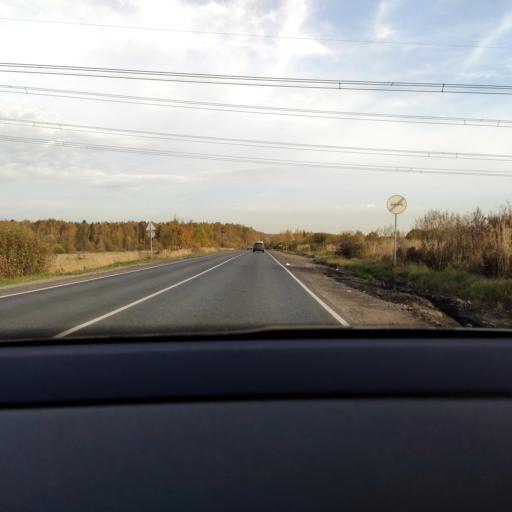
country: RU
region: Moskovskaya
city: Povedniki
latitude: 55.9556
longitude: 37.6408
